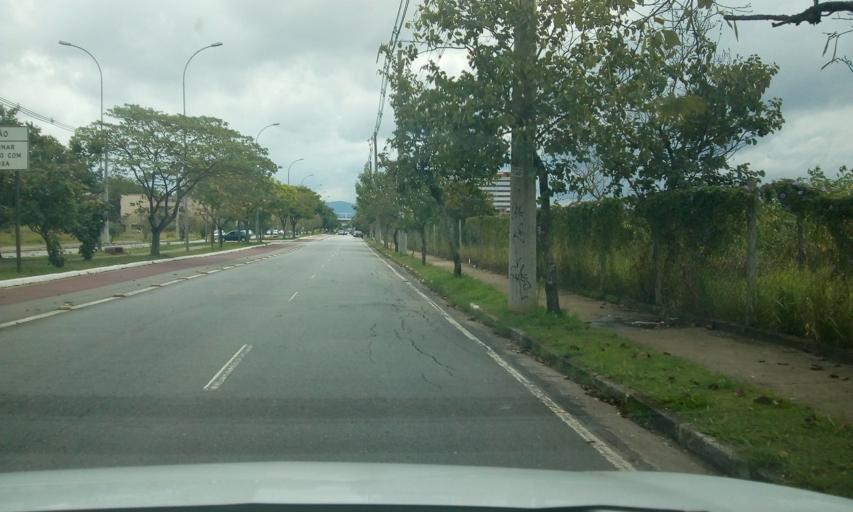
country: BR
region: Sao Paulo
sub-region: Guarulhos
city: Guarulhos
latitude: -23.4540
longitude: -46.4942
